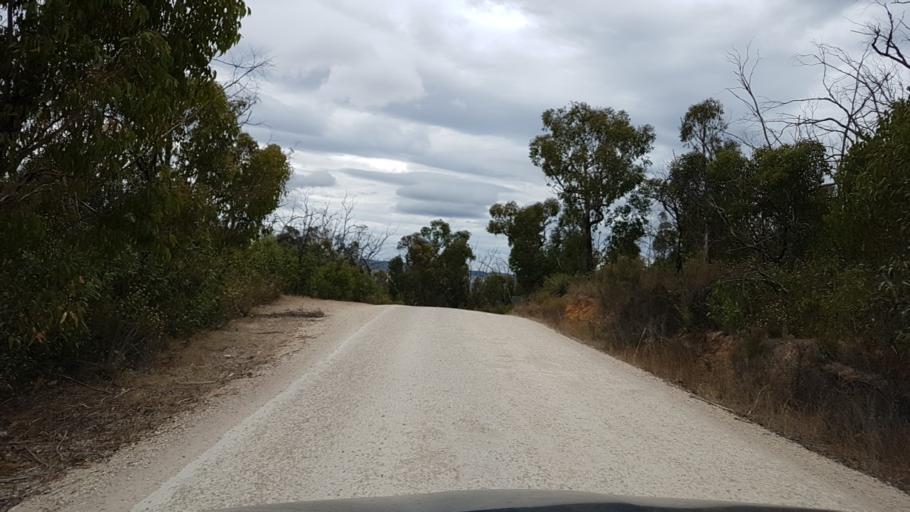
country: AU
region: South Australia
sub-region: Adelaide Hills
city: Gumeracha
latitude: -34.7731
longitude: 138.8198
